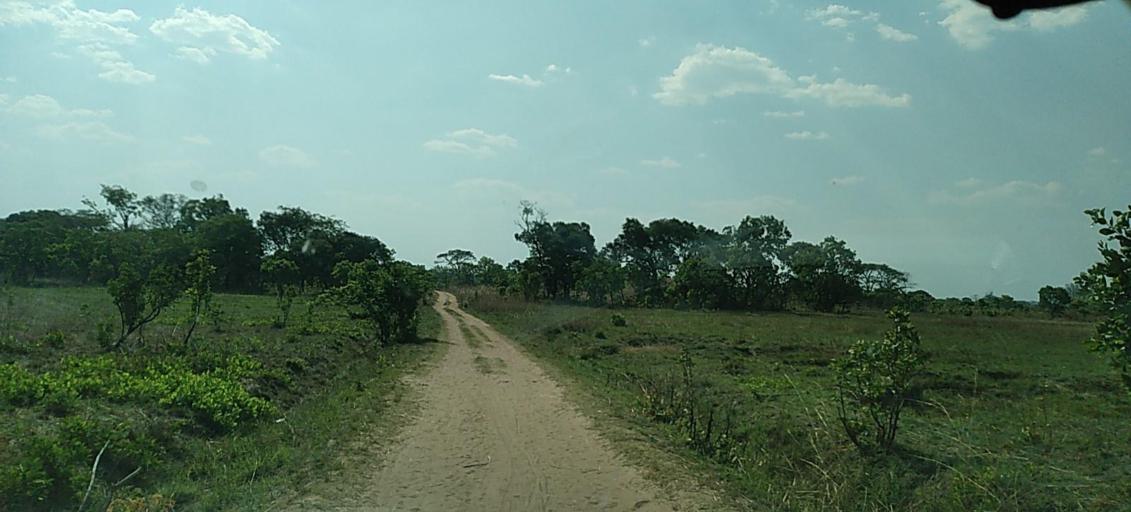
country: ZM
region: North-Western
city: Kalengwa
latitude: -13.1168
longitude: 24.9967
